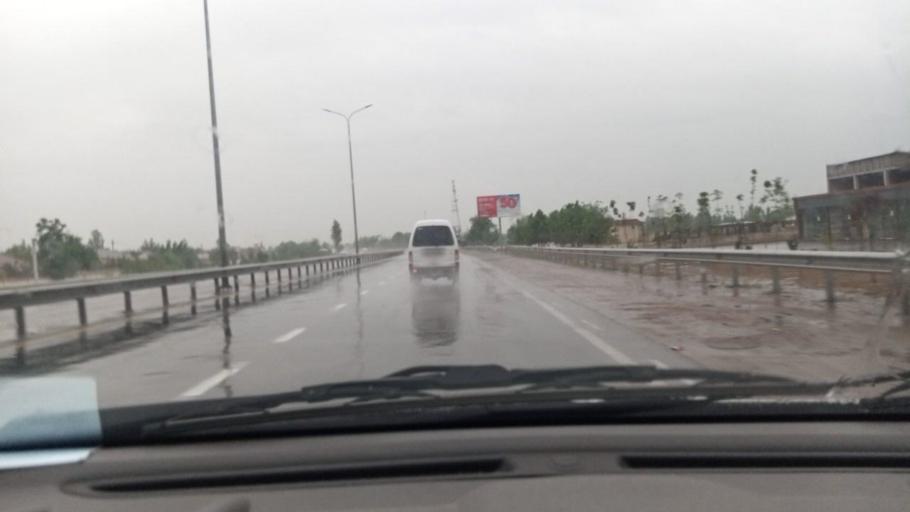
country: UZ
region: Toshkent
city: Tuytepa
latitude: 41.1283
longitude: 69.4370
